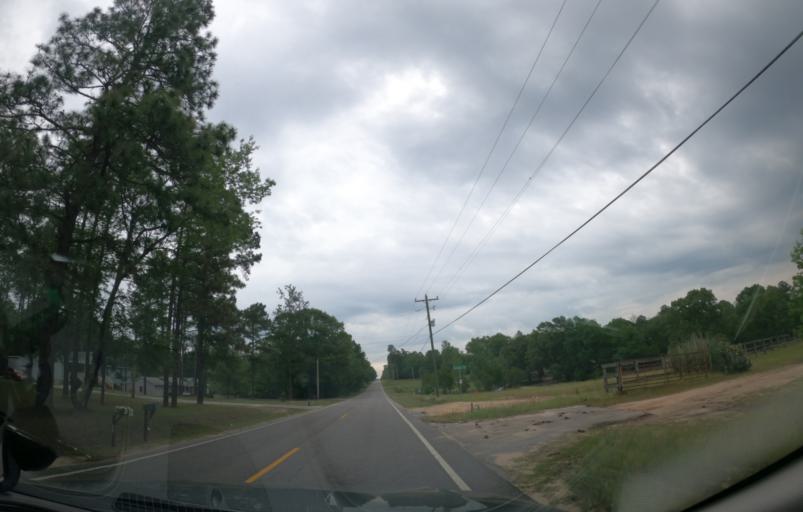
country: US
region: South Carolina
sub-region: Aiken County
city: Aiken
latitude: 33.5720
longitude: -81.6411
